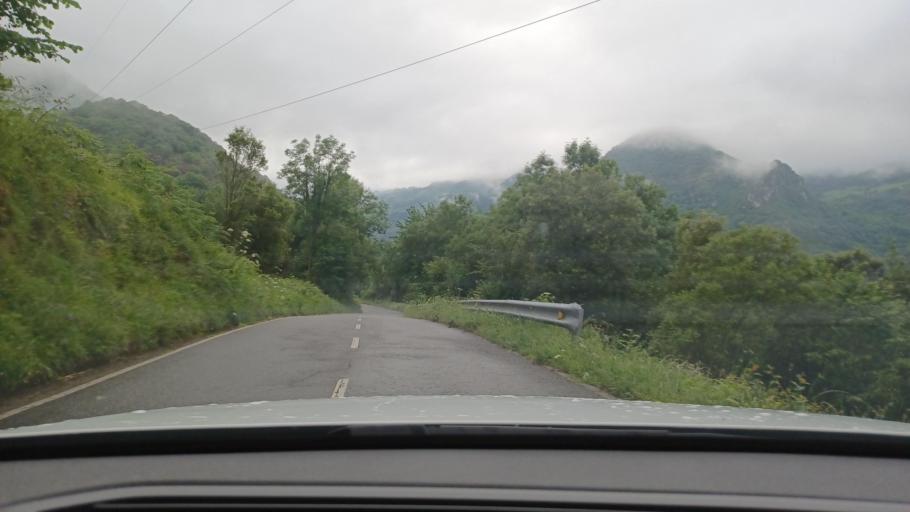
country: ES
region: Asturias
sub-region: Province of Asturias
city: Proaza
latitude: 43.2876
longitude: -5.9779
